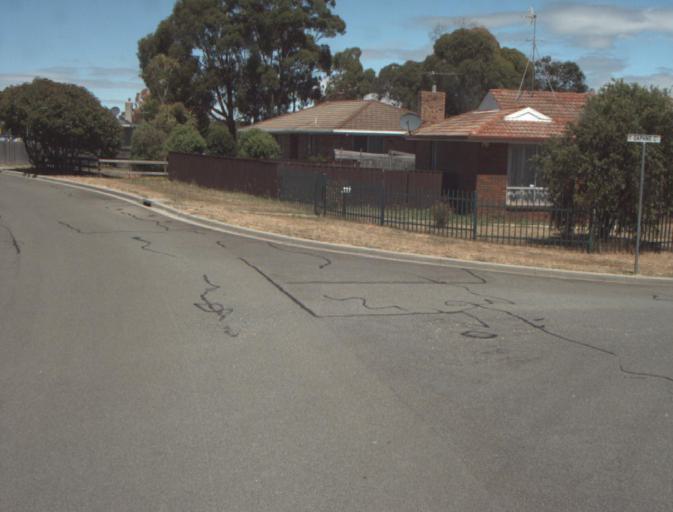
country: AU
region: Tasmania
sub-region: Launceston
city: Mayfield
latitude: -41.3755
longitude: 147.1365
